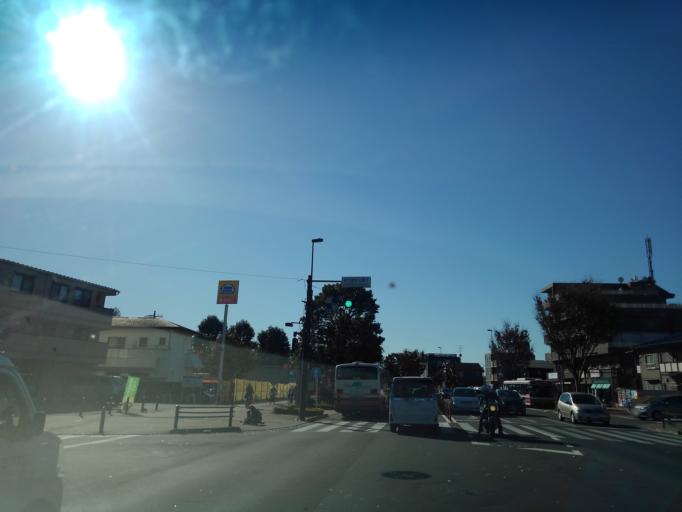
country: JP
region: Tokyo
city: Chofugaoka
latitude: 35.6727
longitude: 139.5448
